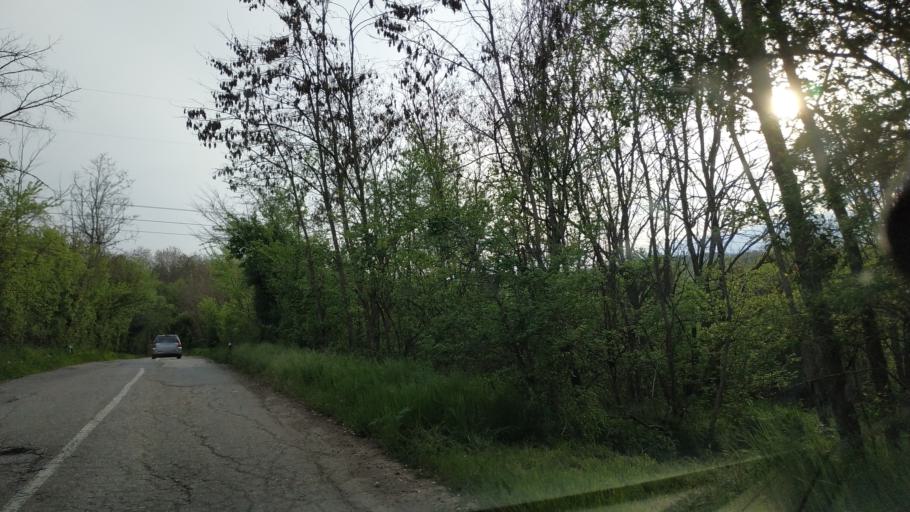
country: RS
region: Central Serbia
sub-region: Nisavski Okrug
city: Aleksinac
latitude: 43.4817
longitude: 21.8147
